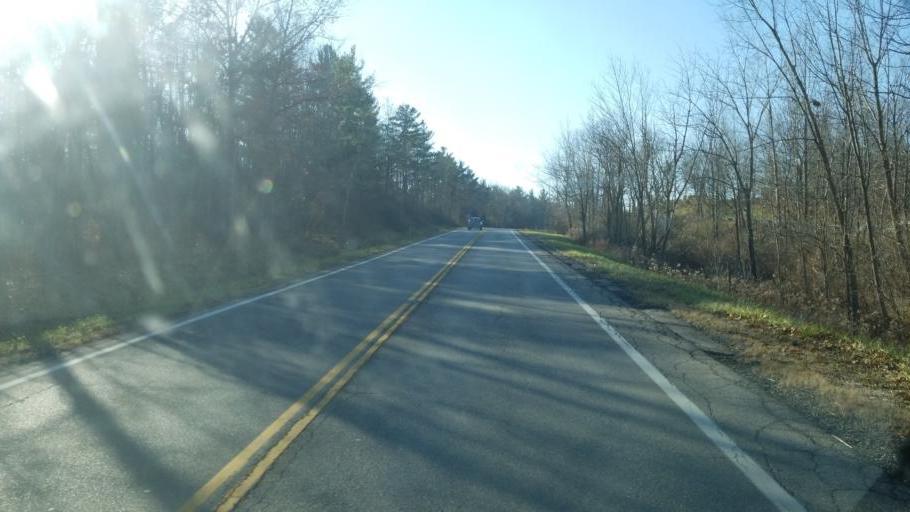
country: US
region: Ohio
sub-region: Geauga County
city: Burton
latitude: 41.4628
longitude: -81.2143
